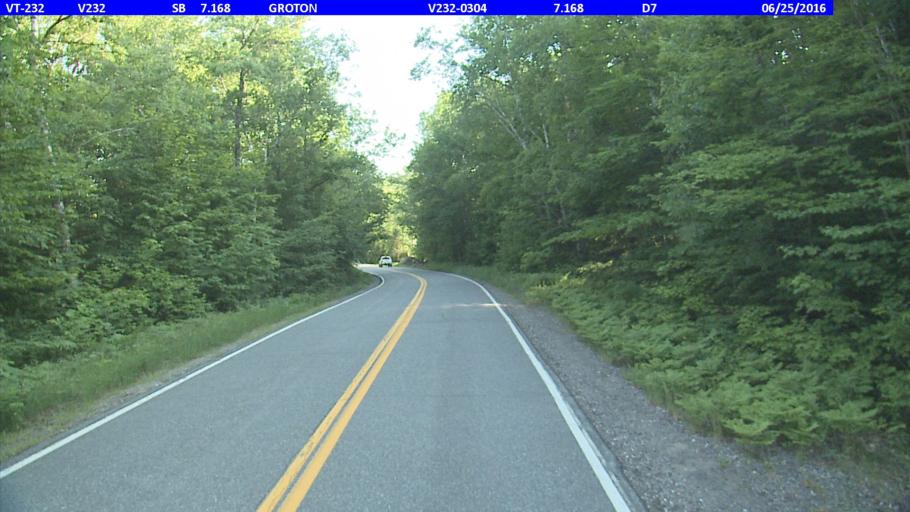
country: US
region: Vermont
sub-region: Caledonia County
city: Hardwick
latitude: 44.2963
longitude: -72.3038
